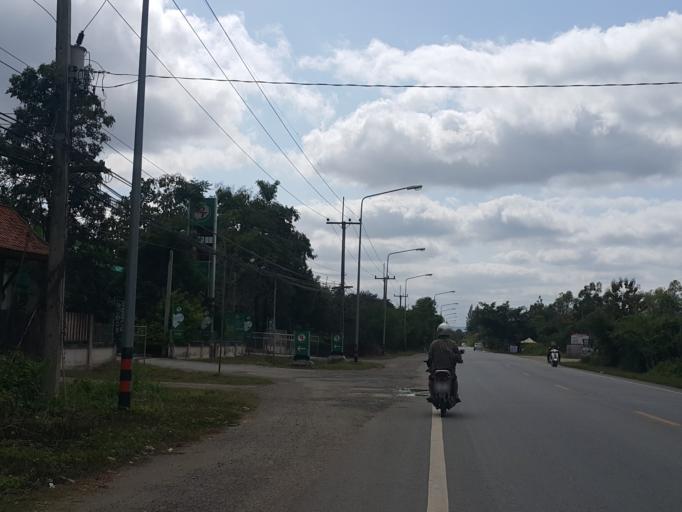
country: TH
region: Lamphun
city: Ban Thi
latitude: 18.6029
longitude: 99.0863
